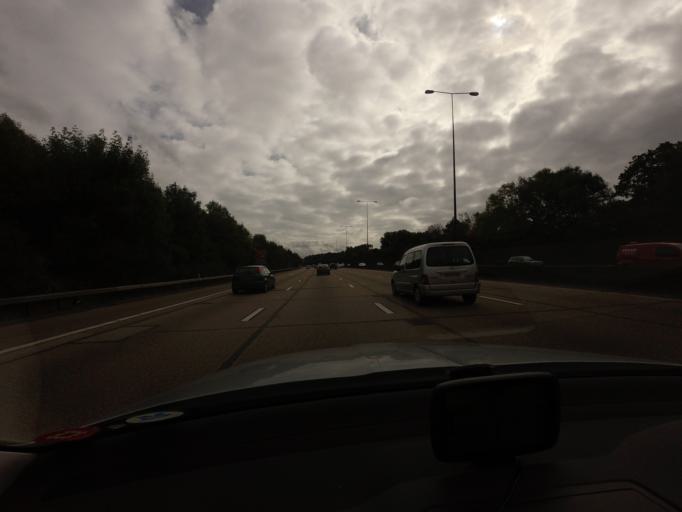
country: GB
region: England
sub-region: Surrey
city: Tadworth
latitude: 51.2623
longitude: -0.2361
